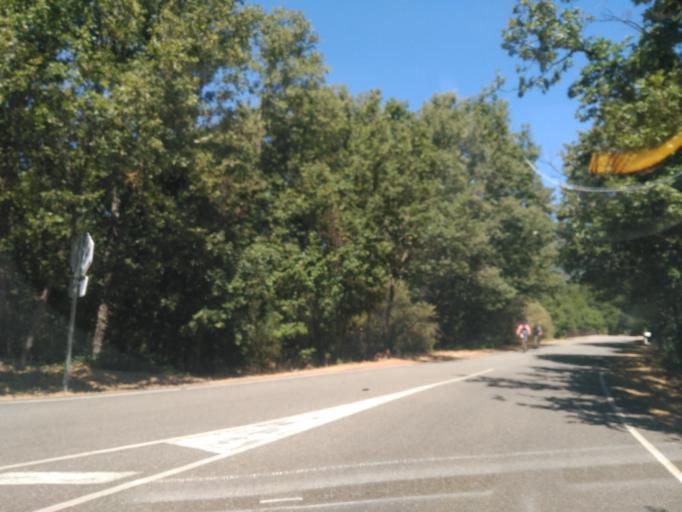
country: ES
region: Castille and Leon
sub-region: Provincia de Zamora
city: Galende
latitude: 42.1193
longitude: -6.6981
